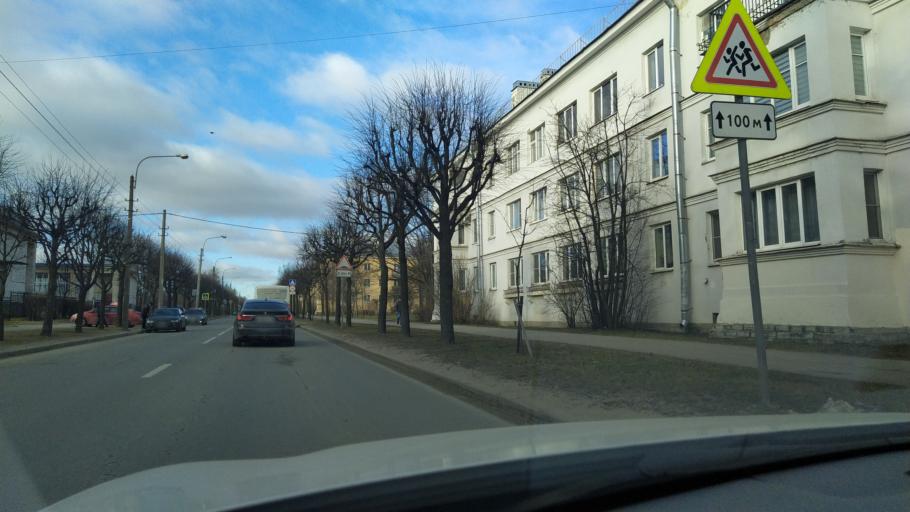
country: RU
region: St.-Petersburg
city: Pushkin
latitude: 59.7241
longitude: 30.4254
